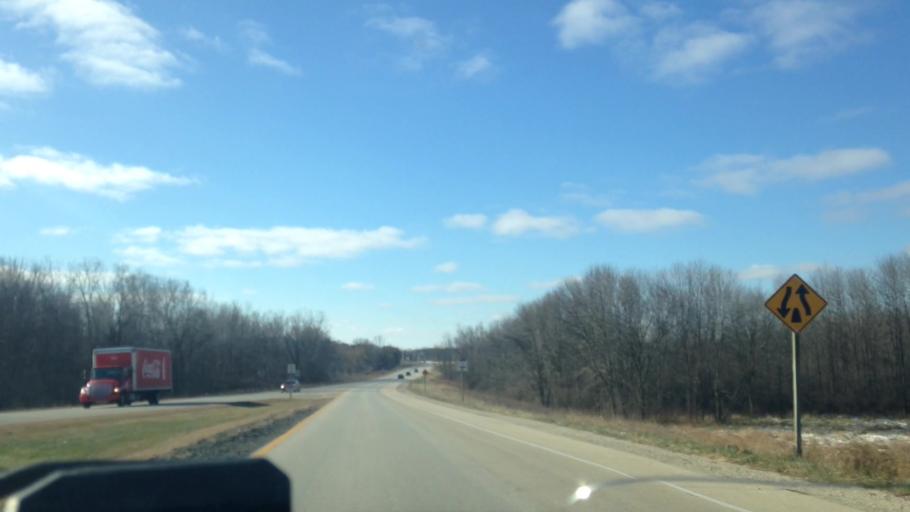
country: US
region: Wisconsin
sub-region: Washington County
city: Germantown
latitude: 43.2115
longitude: -88.1510
